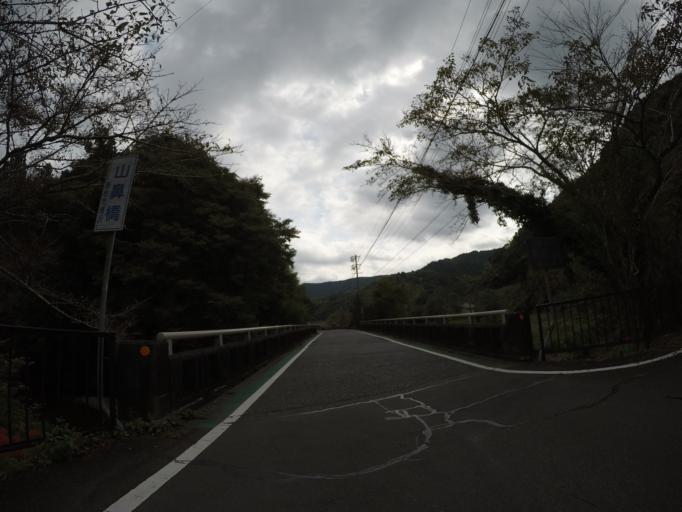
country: JP
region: Shizuoka
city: Fujieda
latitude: 34.9064
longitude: 138.1953
